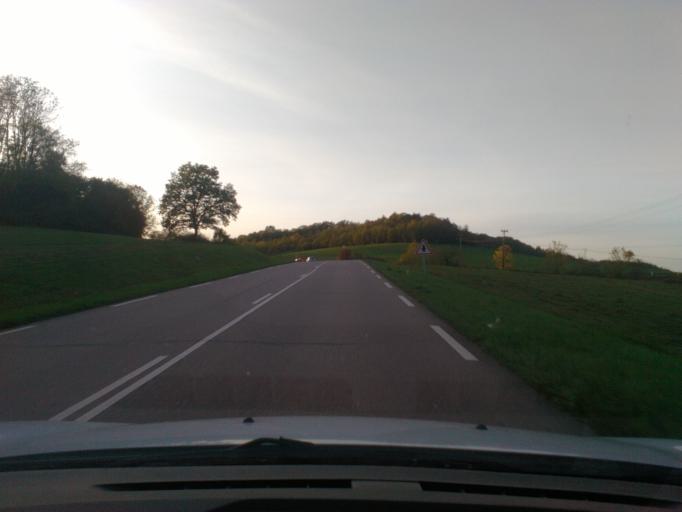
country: FR
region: Lorraine
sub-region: Departement des Vosges
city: Vincey
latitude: 48.3452
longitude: 6.3055
